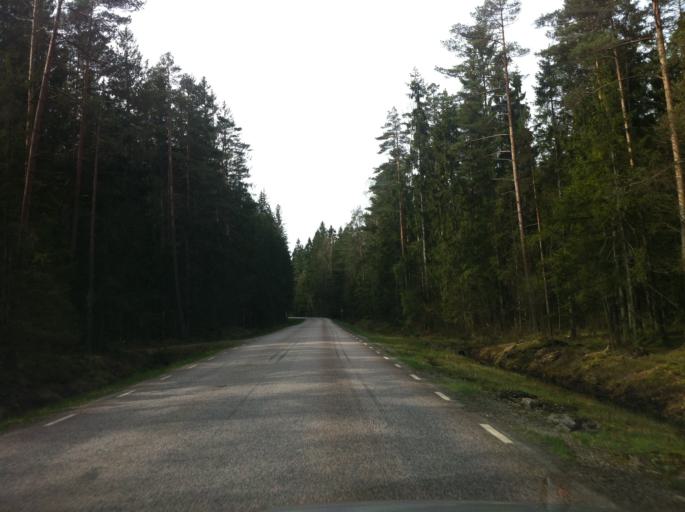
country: SE
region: Vaestra Goetaland
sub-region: Bollebygds Kommun
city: Bollebygd
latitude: 57.6001
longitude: 12.5887
